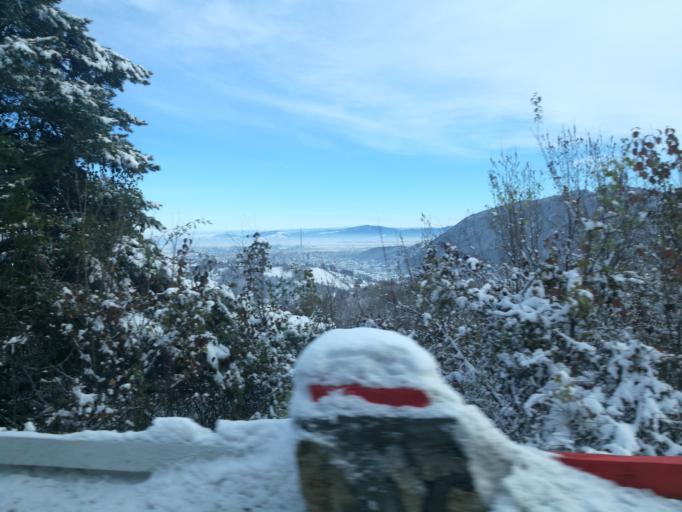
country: RO
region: Brasov
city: Brasov
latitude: 45.6369
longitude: 25.5646
